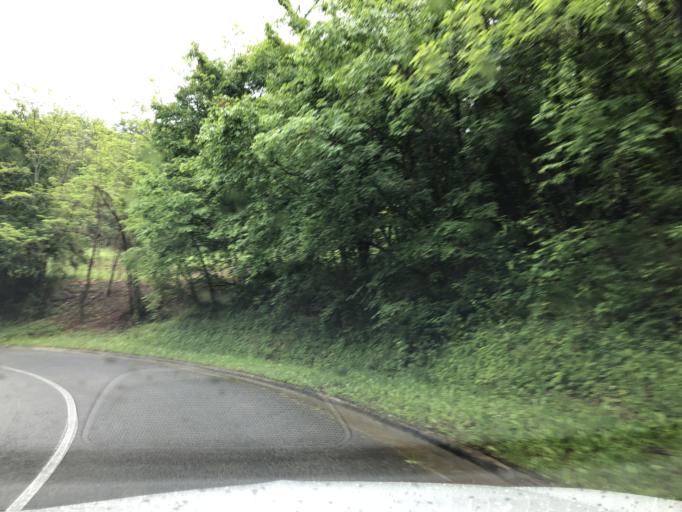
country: SI
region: Koper-Capodistria
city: Prade
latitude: 45.5025
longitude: 13.7725
